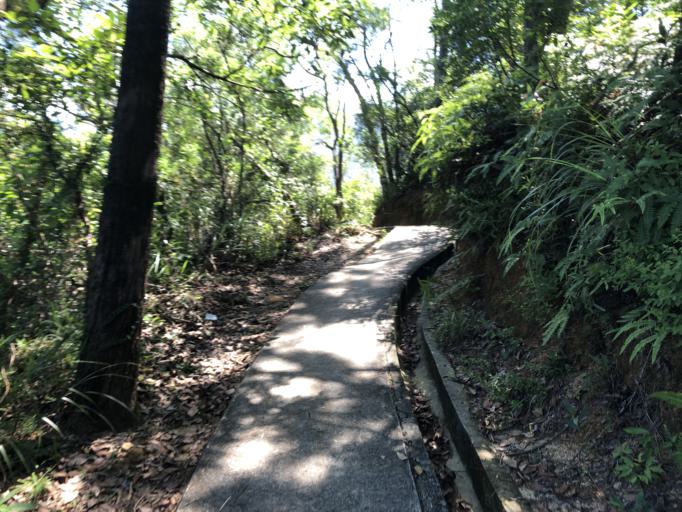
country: HK
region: Tuen Mun
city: Tuen Mun
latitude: 22.2794
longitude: 113.9880
